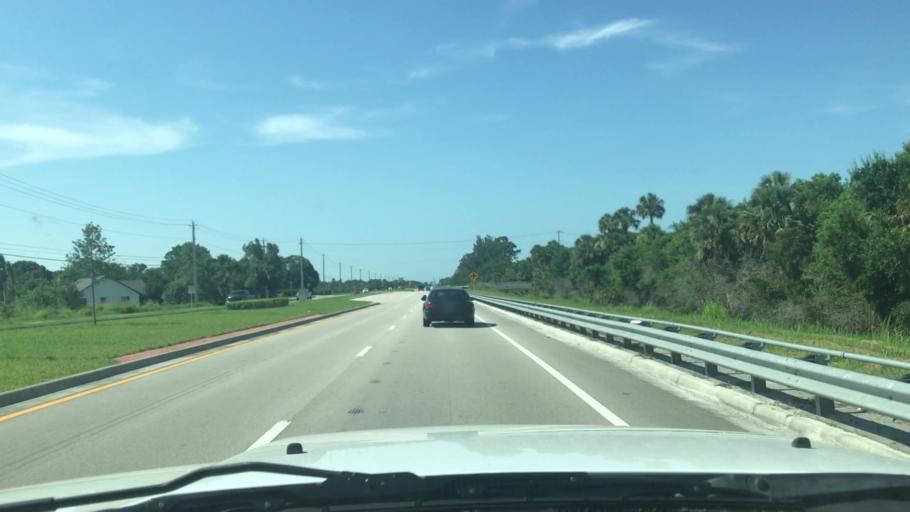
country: US
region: Florida
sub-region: Indian River County
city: West Vero Corridor
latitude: 27.6588
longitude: -80.4630
